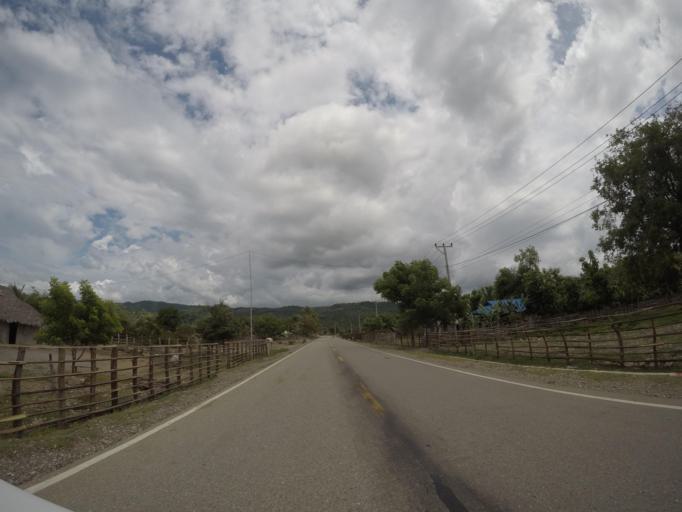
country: TL
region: Bobonaro
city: Maliana
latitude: -8.8278
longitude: 125.0677
